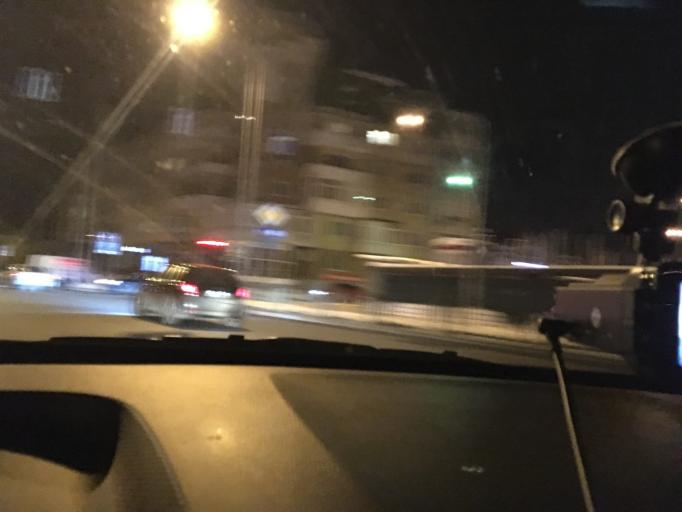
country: RU
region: Tjumen
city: Tyumen
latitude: 57.1576
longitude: 65.5413
